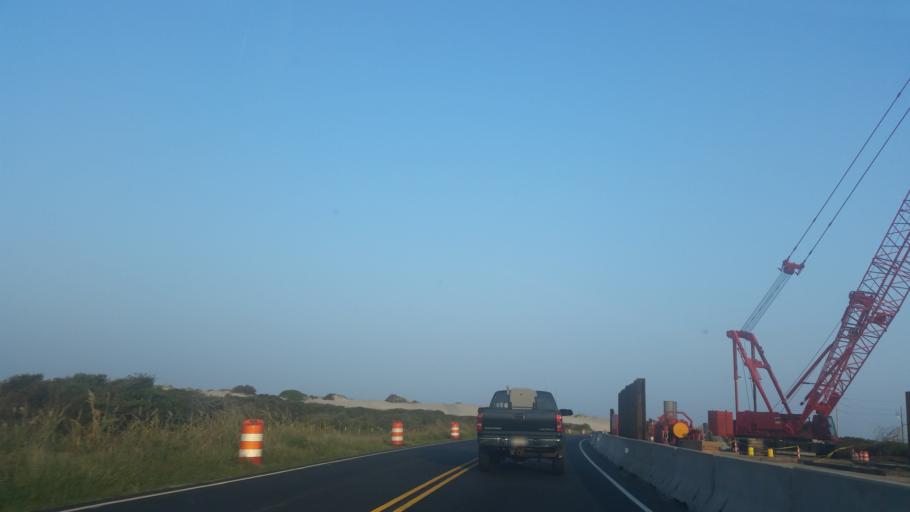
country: US
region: North Carolina
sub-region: Dare County
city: Wanchese
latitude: 35.7661
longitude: -75.5229
